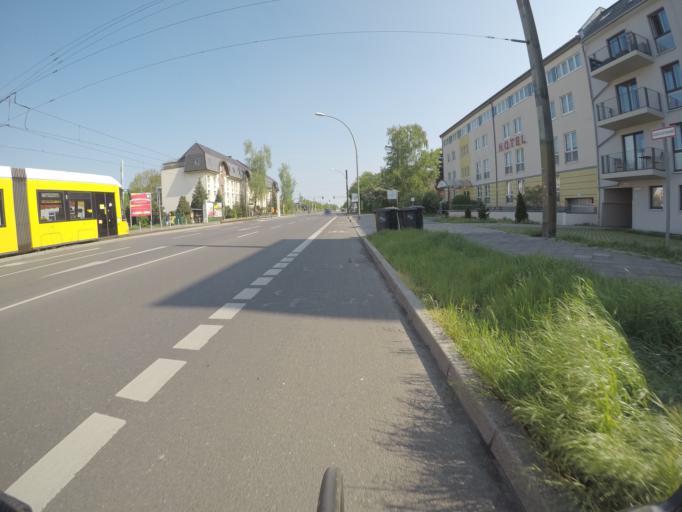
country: DE
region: Berlin
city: Buchholz
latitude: 52.5888
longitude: 13.4304
